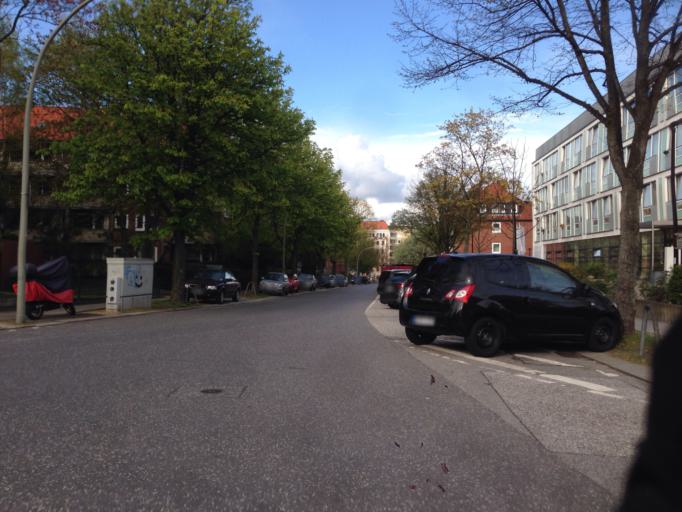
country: DE
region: Hamburg
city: Borgfelde
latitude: 53.5603
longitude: 10.0333
